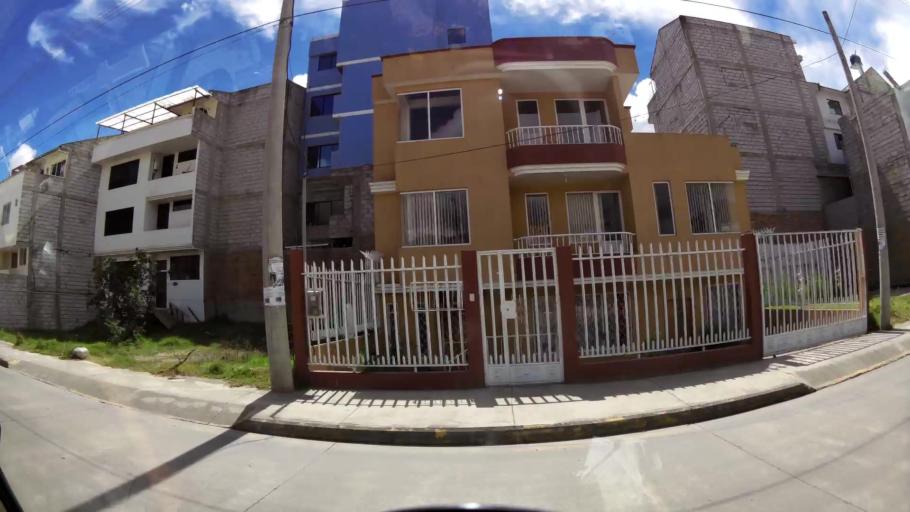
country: EC
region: Canar
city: Azogues
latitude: -2.7430
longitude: -78.8518
